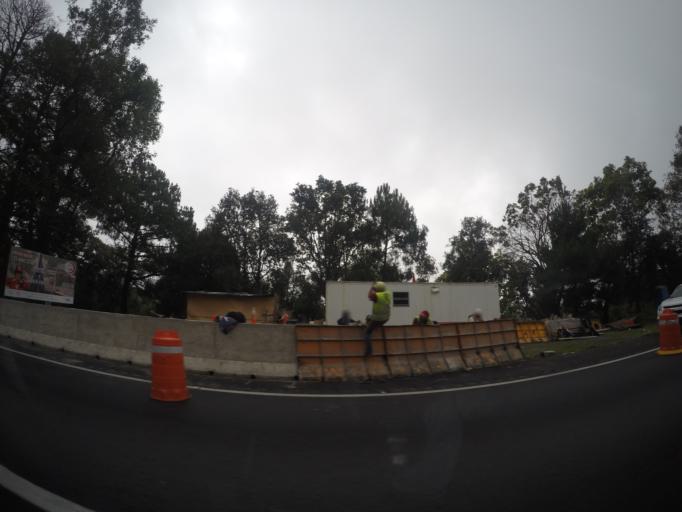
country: MX
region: Morelos
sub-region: Cuernavaca
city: Villa Santiago
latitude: 19.0279
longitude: -99.1823
